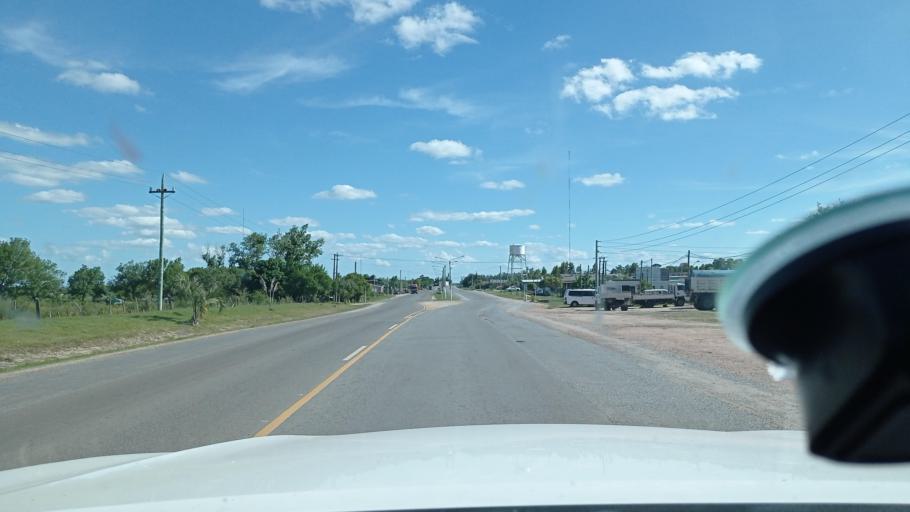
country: UY
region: Florida
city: Florida
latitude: -34.0843
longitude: -56.2367
